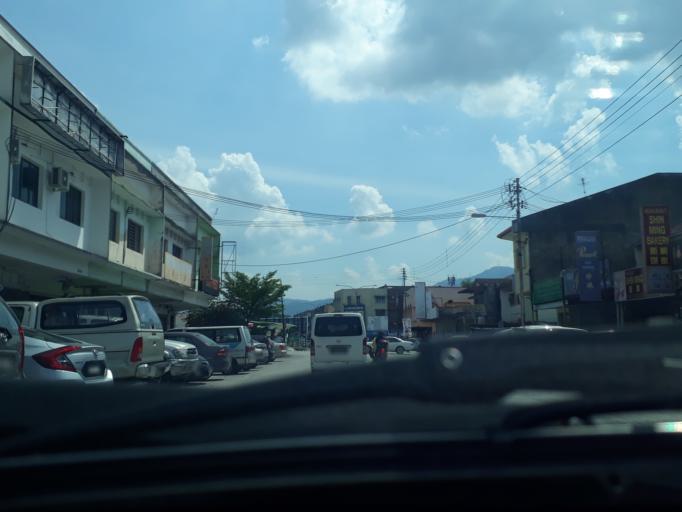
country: MY
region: Perak
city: Ipoh
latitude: 4.5822
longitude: 101.0836
